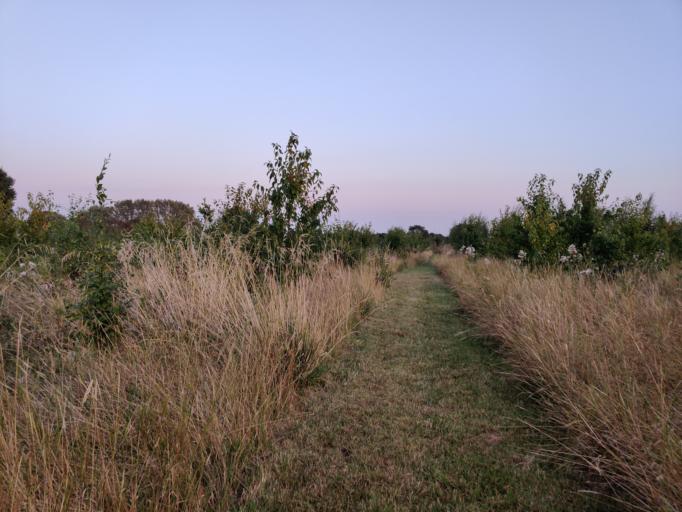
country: DK
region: South Denmark
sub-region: AEro Kommune
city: AEroskobing
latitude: 54.8970
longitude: 10.3121
